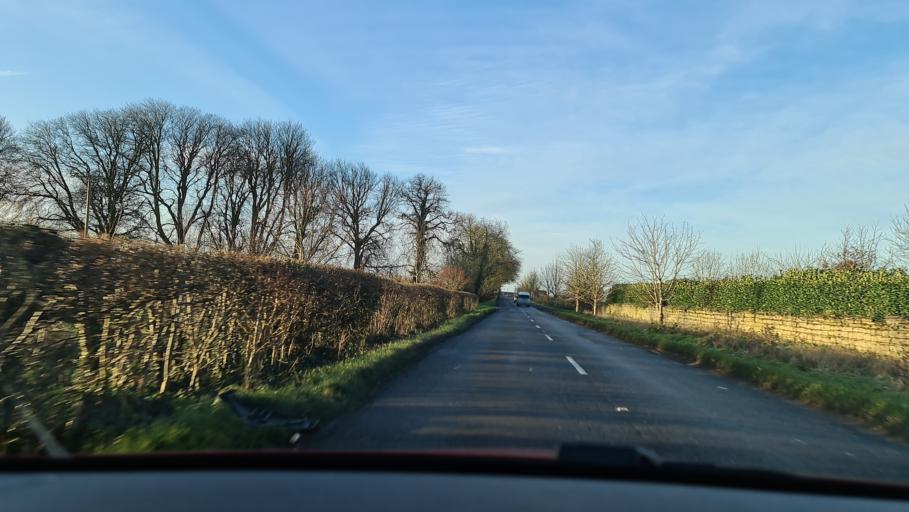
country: GB
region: England
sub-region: Buckinghamshire
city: Waddesdon
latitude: 51.8232
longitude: -0.9169
